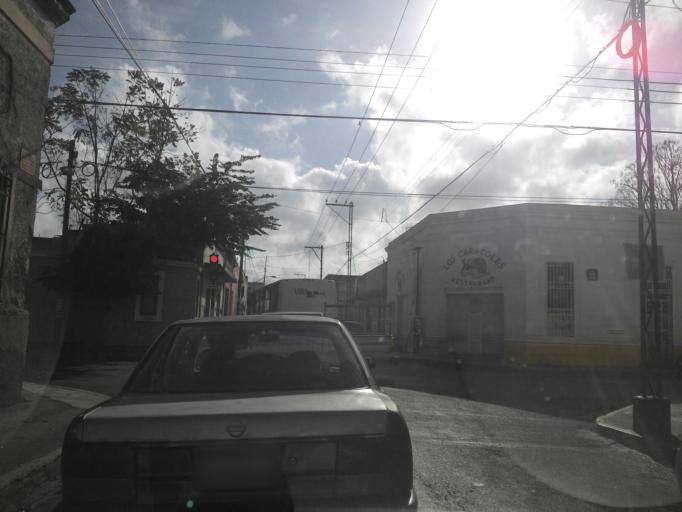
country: MX
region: Yucatan
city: Merida
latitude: 20.9640
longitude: -89.6292
